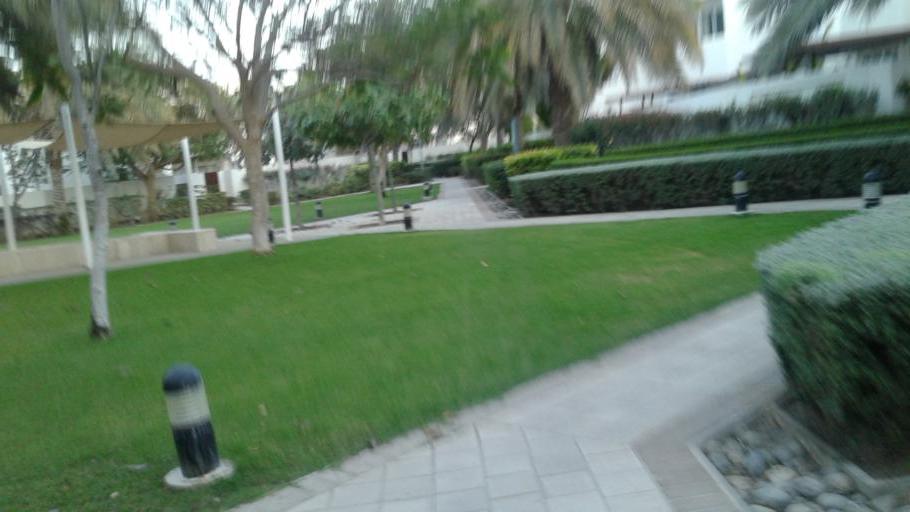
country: OM
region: Muhafazat Masqat
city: As Sib al Jadidah
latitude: 23.6266
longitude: 58.2700
